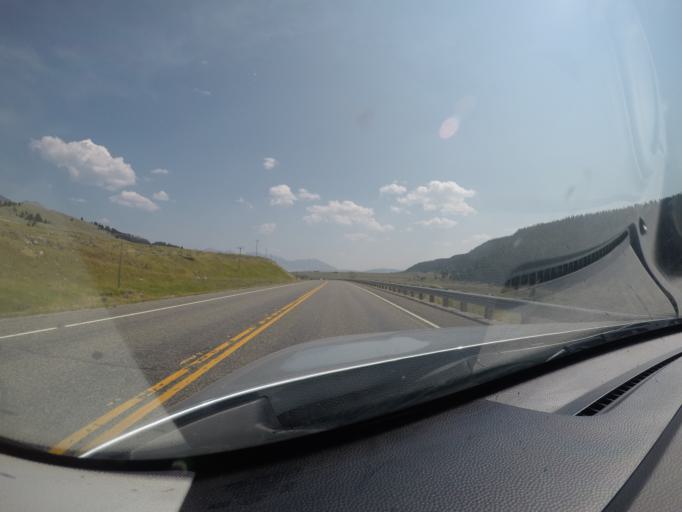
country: US
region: Montana
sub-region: Gallatin County
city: Big Sky
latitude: 44.8724
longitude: -111.5647
